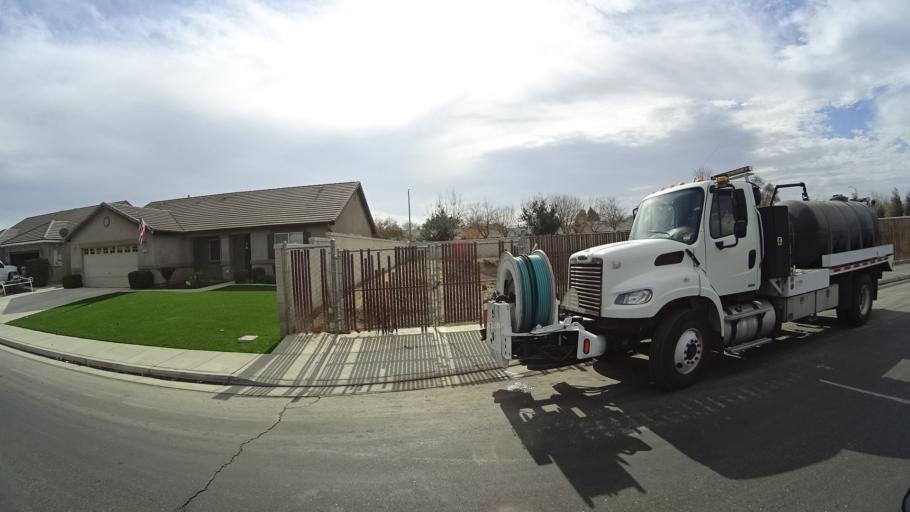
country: US
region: California
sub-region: Kern County
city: Rosedale
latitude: 35.4203
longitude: -119.1399
